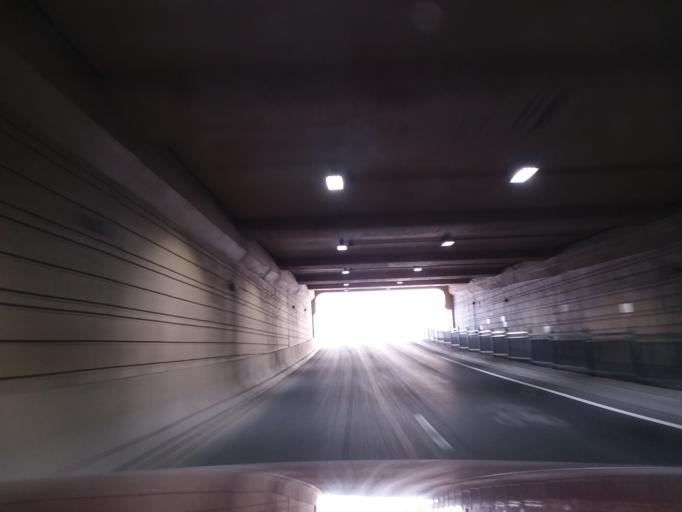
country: US
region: Nevada
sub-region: Clark County
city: Las Vegas
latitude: 36.1733
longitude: -115.1468
